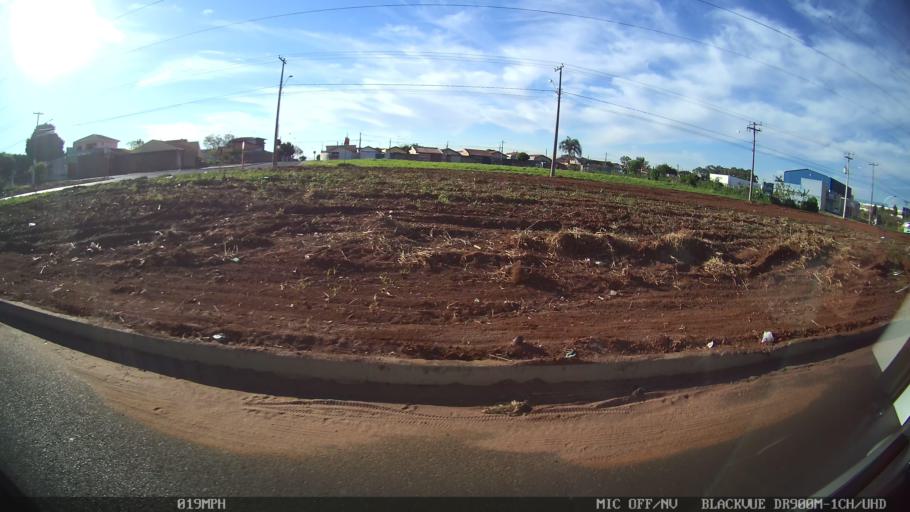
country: BR
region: Sao Paulo
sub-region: Americo Brasiliense
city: Americo Brasiliense
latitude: -21.7475
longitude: -48.1400
